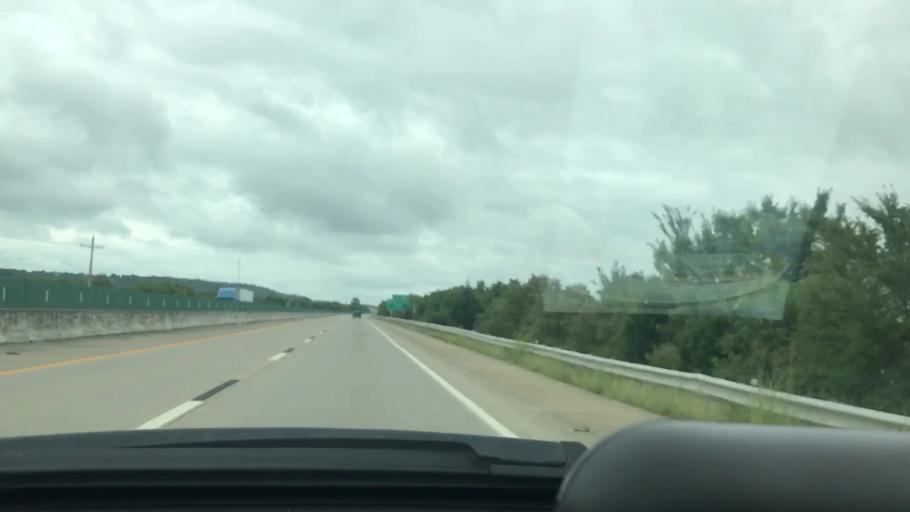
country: US
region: Oklahoma
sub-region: Pittsburg County
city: Krebs
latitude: 35.0459
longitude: -95.7102
